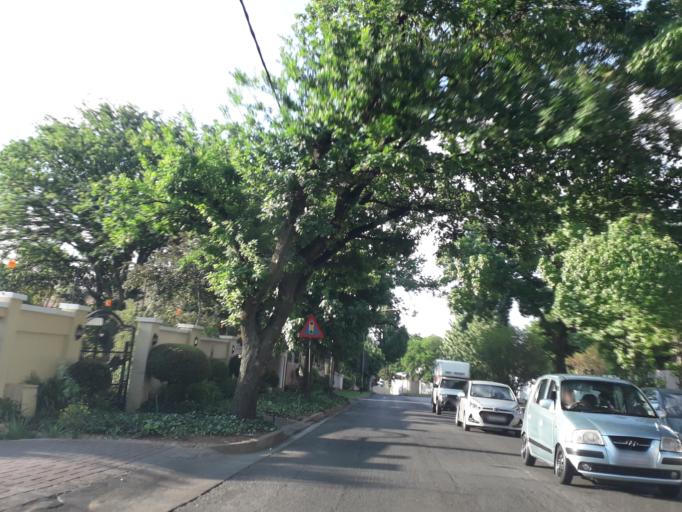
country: ZA
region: Gauteng
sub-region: City of Johannesburg Metropolitan Municipality
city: Johannesburg
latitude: -26.1479
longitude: 28.0063
